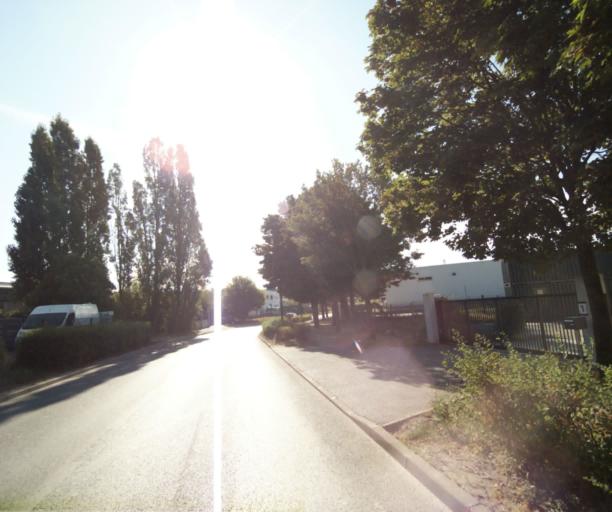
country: FR
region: Ile-de-France
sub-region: Departement de Seine-et-Marne
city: Saint-Thibault-des-Vignes
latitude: 48.8711
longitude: 2.6788
